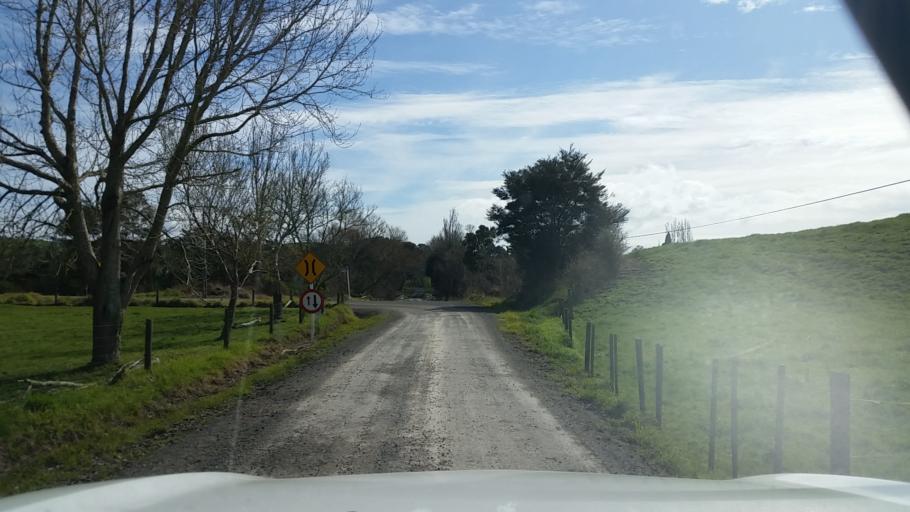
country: NZ
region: Waikato
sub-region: Hauraki District
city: Ngatea
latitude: -37.4449
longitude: 175.4877
